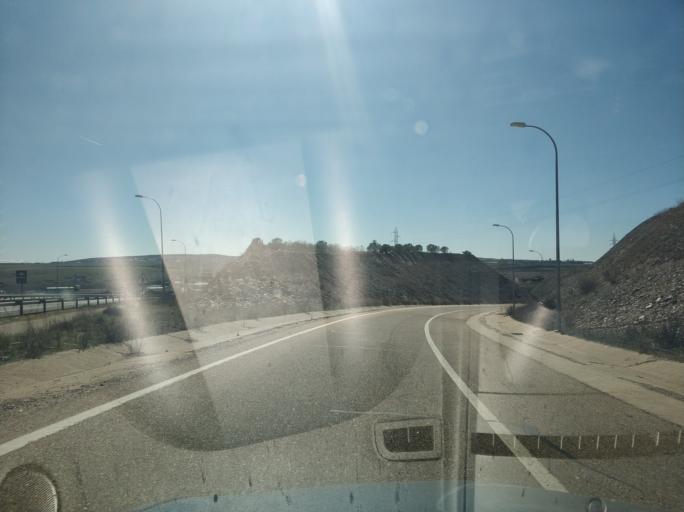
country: ES
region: Castille and Leon
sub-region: Provincia de Salamanca
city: Villamayor
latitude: 40.9652
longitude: -5.7003
